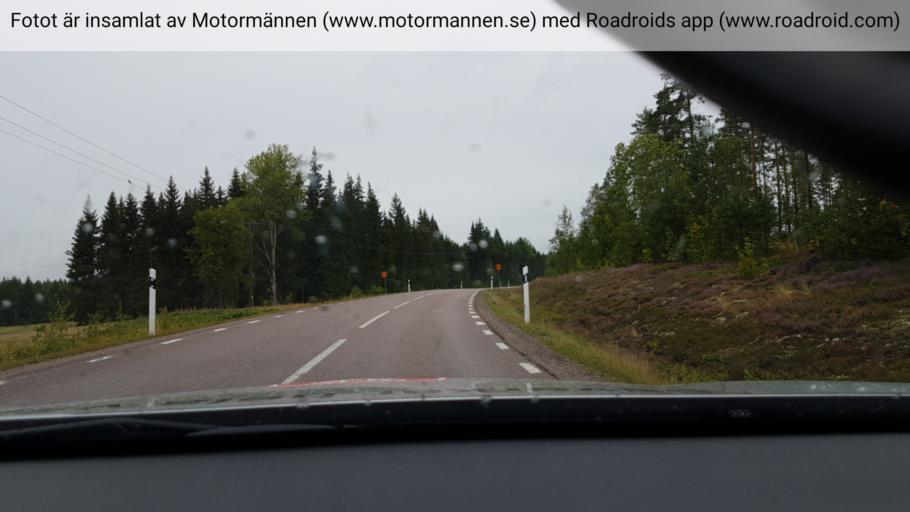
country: SE
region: Gaevleborg
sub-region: Gavle Kommun
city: Hedesunda
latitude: 60.4879
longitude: 16.9363
